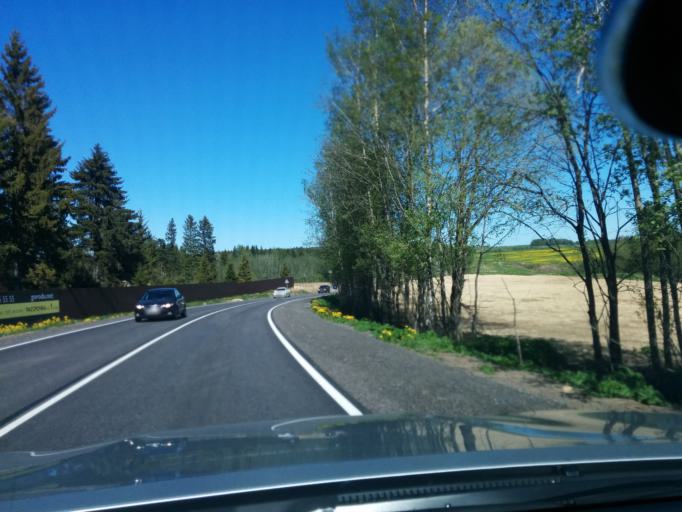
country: RU
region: Leningrad
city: Verkhniye Osel'ki
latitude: 60.1811
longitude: 30.3833
